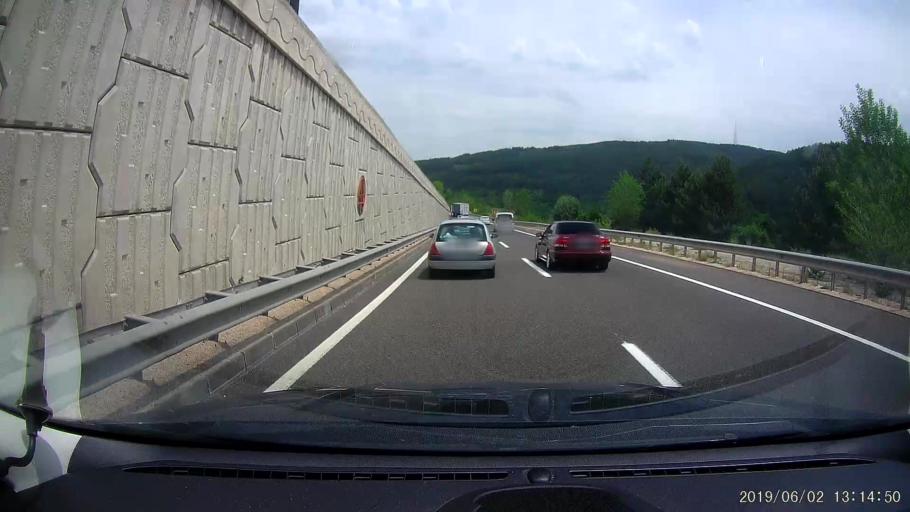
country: TR
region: Karabuk
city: Gozyeri
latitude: 40.8420
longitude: 32.6544
